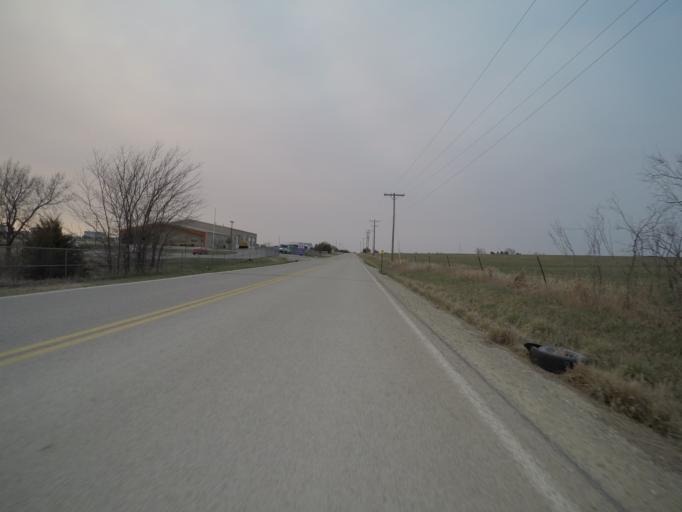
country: US
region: Kansas
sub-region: Riley County
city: Manhattan
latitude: 39.2477
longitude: -96.6538
